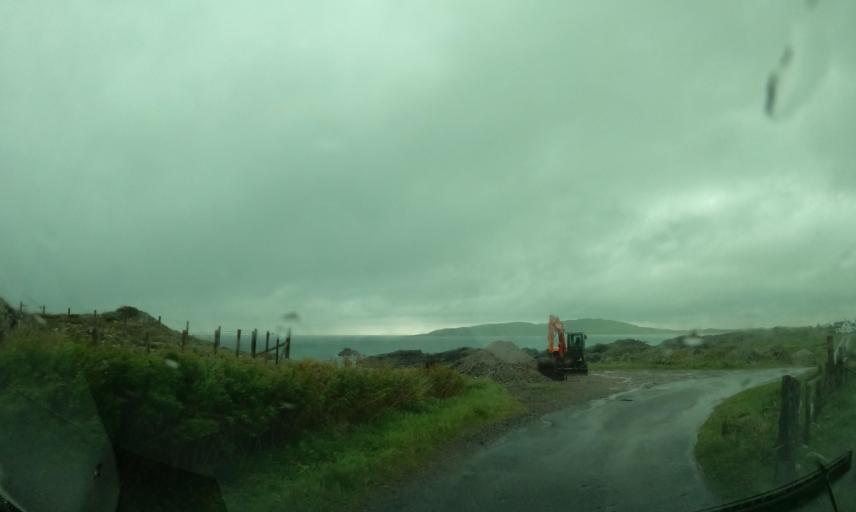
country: GB
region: Scotland
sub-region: Eilean Siar
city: Barra
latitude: 56.4515
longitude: -6.9376
